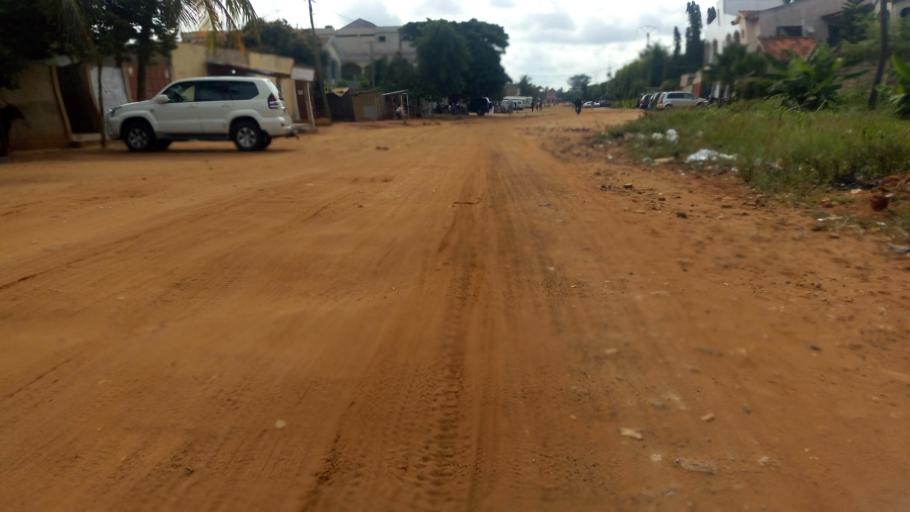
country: TG
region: Maritime
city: Lome
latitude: 6.2189
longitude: 1.1938
